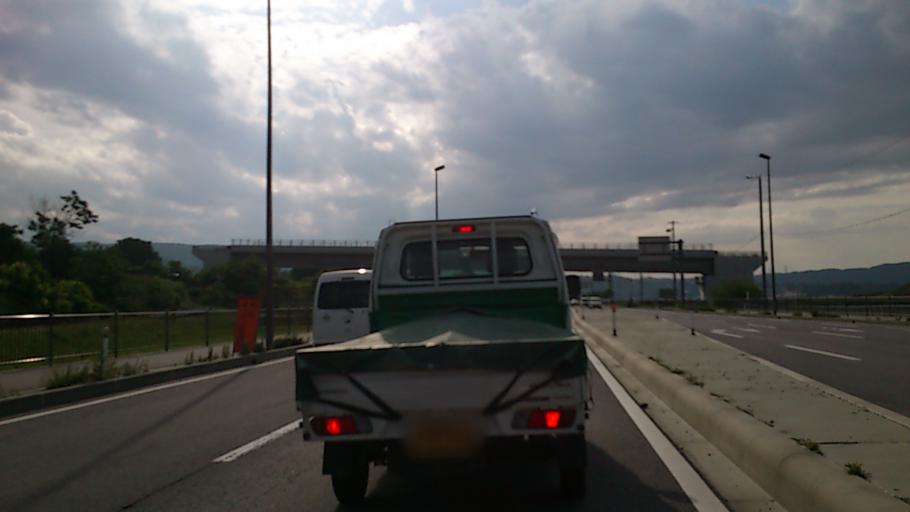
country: JP
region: Nagano
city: Saku
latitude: 36.2376
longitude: 138.4394
